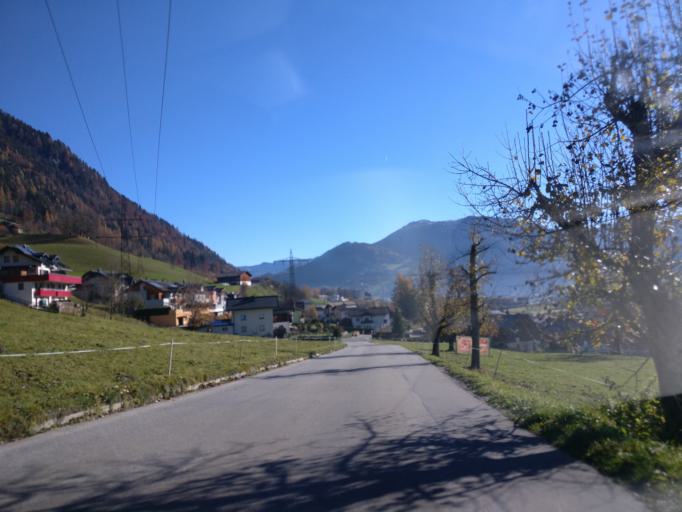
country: AT
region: Salzburg
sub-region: Politischer Bezirk Sankt Johann im Pongau
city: Sankt Veit im Pongau
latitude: 47.3337
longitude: 13.1493
